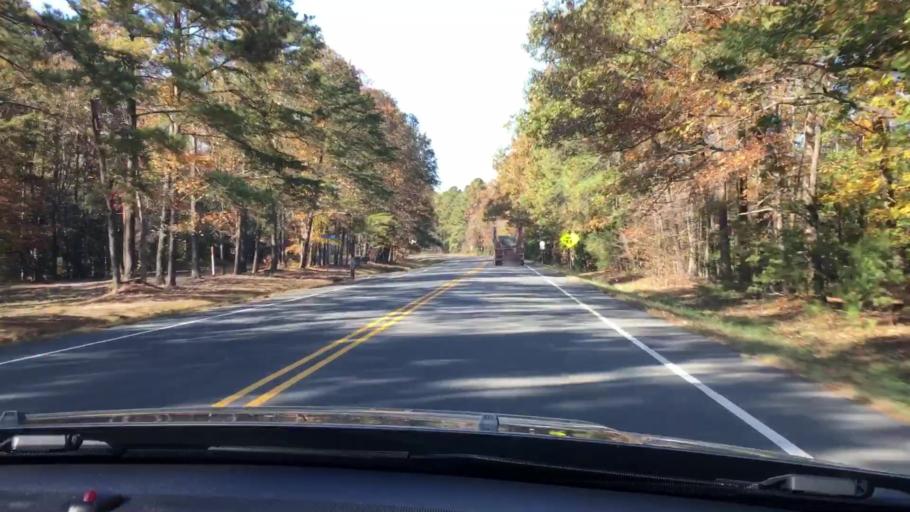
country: US
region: Virginia
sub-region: King William County
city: Central Garage
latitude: 37.7825
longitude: -77.1689
